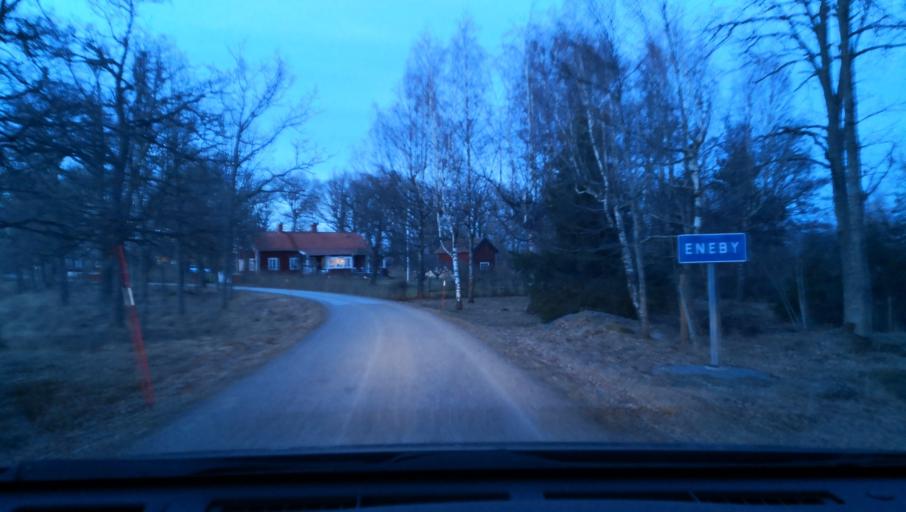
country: SE
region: Uppsala
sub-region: Enkopings Kommun
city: Dalby
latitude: 59.5540
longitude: 17.3704
